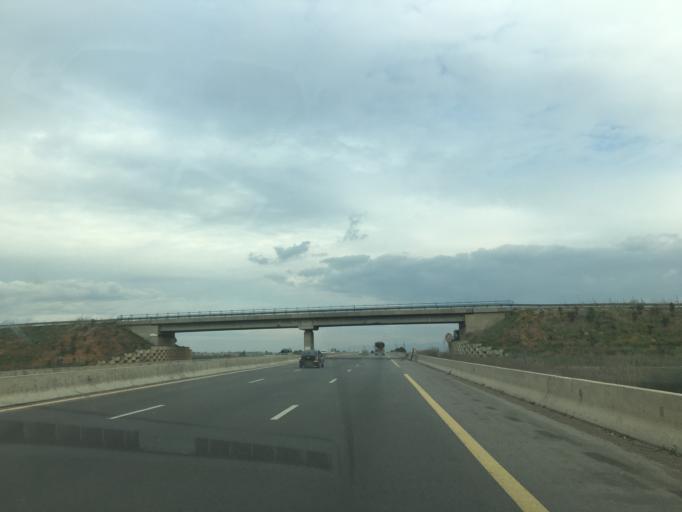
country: DZ
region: Bouira
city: Bouira
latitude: 36.3277
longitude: 3.9709
